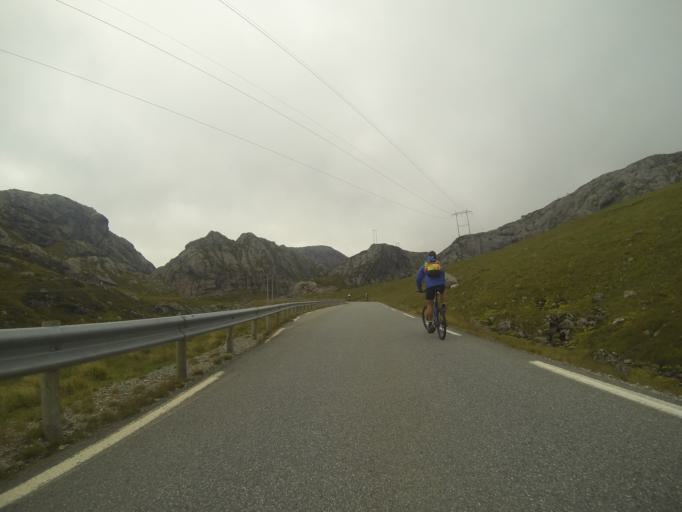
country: NO
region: Vest-Agder
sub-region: Sirdal
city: Tonstad
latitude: 59.0330
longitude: 6.6533
